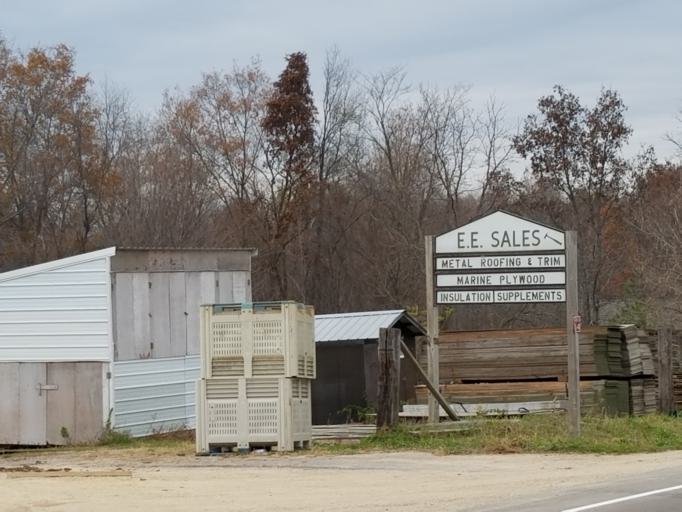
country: US
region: Wisconsin
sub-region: Vernon County
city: Hillsboro
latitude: 43.6392
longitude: -90.4525
